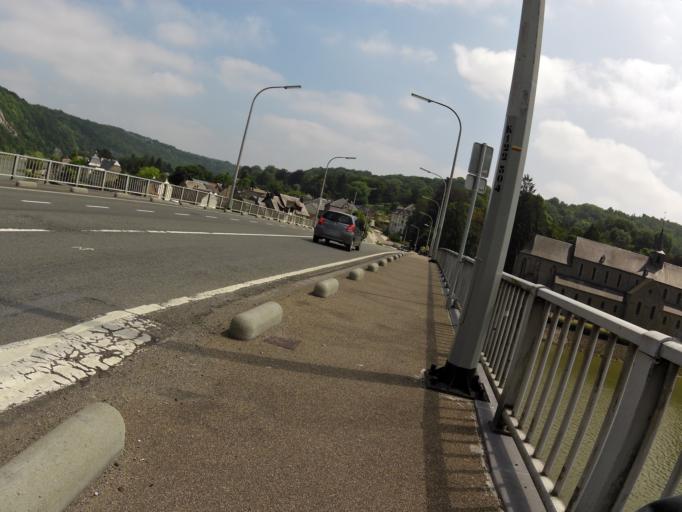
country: BE
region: Wallonia
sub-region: Province de Namur
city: Hastiere-Lavaux
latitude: 50.2160
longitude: 4.8264
